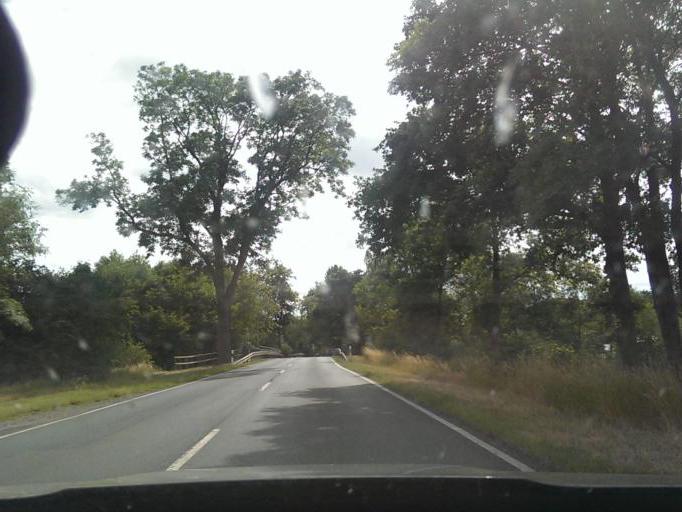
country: DE
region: Lower Saxony
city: Essel
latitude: 52.6932
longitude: 9.6473
